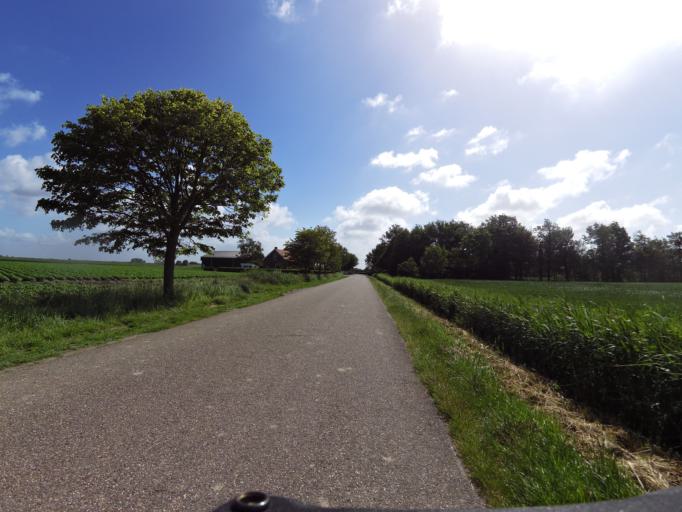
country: NL
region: Zeeland
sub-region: Schouwen-Duiveland
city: Scharendijke
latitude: 51.6934
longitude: 3.9417
